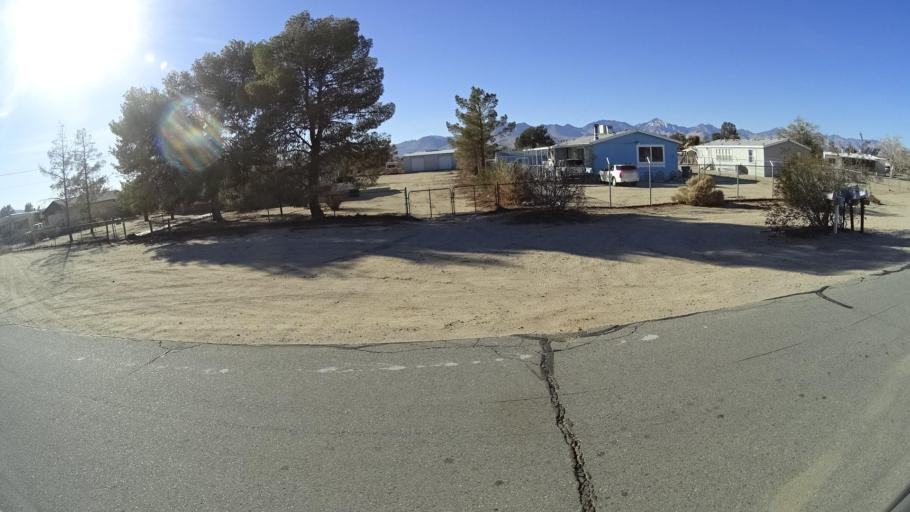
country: US
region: California
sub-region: Kern County
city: China Lake Acres
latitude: 35.6398
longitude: -117.7585
